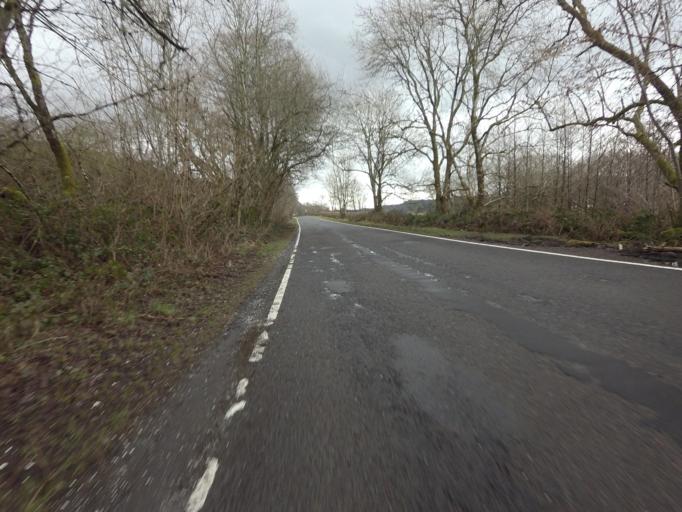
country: GB
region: Scotland
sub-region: Stirling
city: Killearn
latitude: 56.1882
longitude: -4.4881
